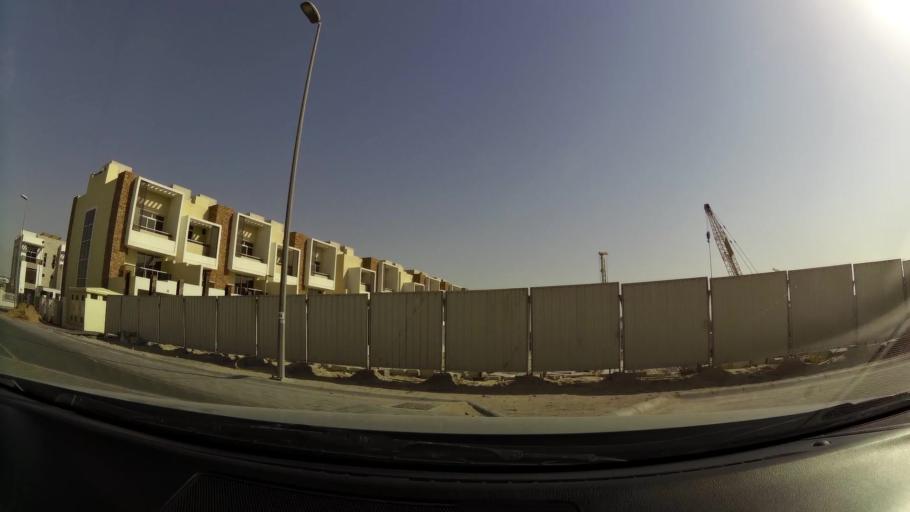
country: AE
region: Dubai
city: Dubai
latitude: 25.0652
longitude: 55.2029
